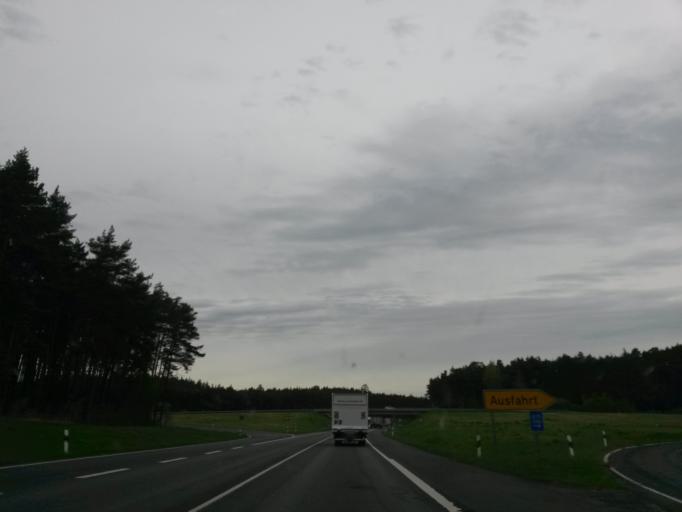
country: DE
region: Bavaria
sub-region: Upper Franconia
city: Pommersfelden
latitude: 49.7419
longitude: 10.8274
